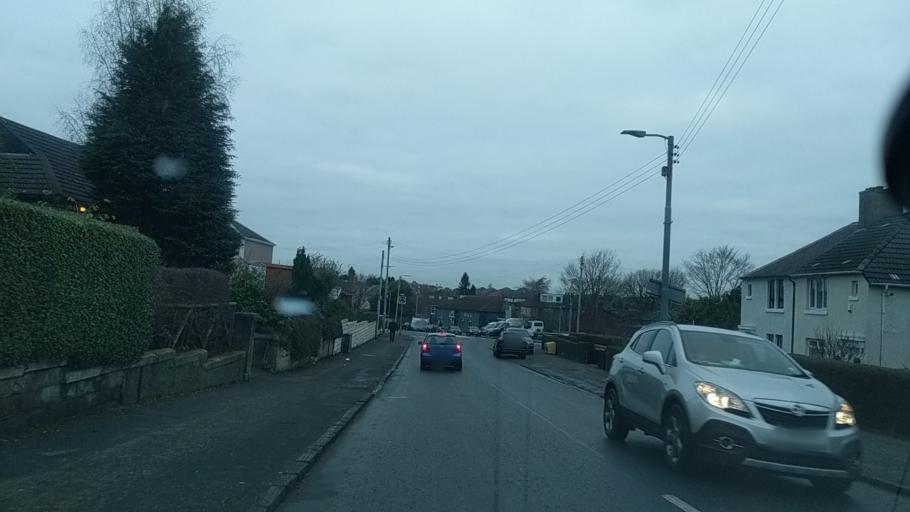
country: GB
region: Scotland
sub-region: South Lanarkshire
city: Rutherglen
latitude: 55.8179
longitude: -4.1902
